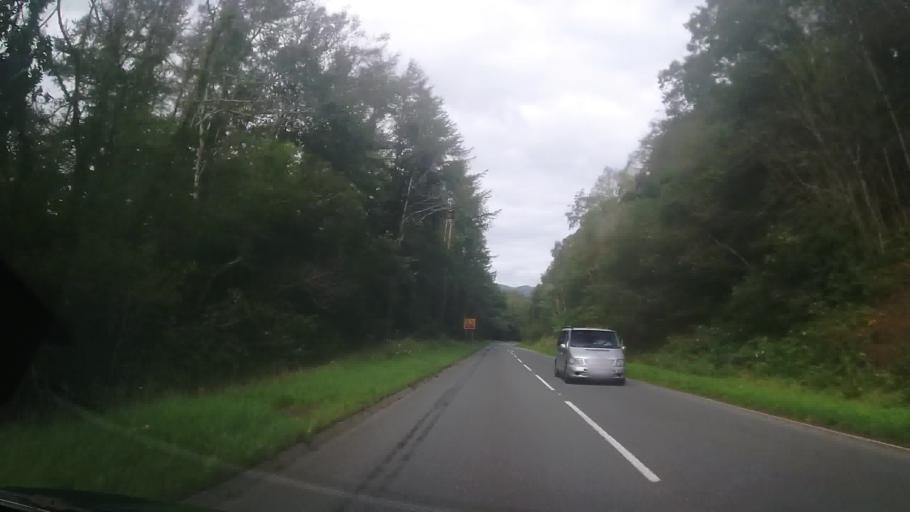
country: GB
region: Wales
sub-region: Gwynedd
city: Barmouth
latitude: 52.7290
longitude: -3.9810
